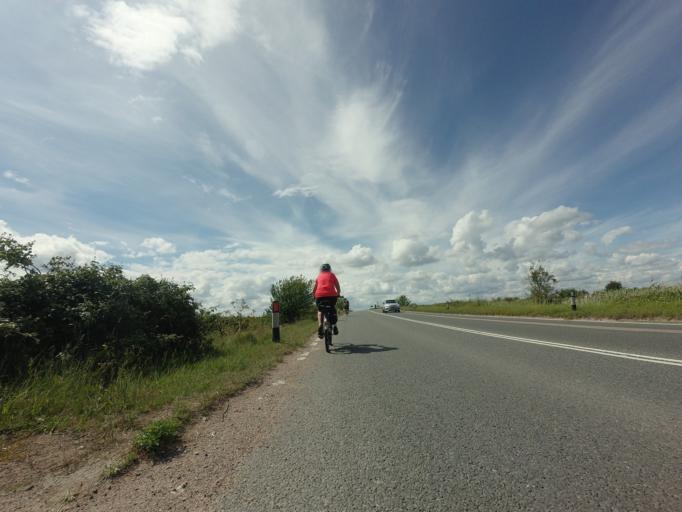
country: GB
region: England
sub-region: Medway
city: Allhallows
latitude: 51.4472
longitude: 0.6745
